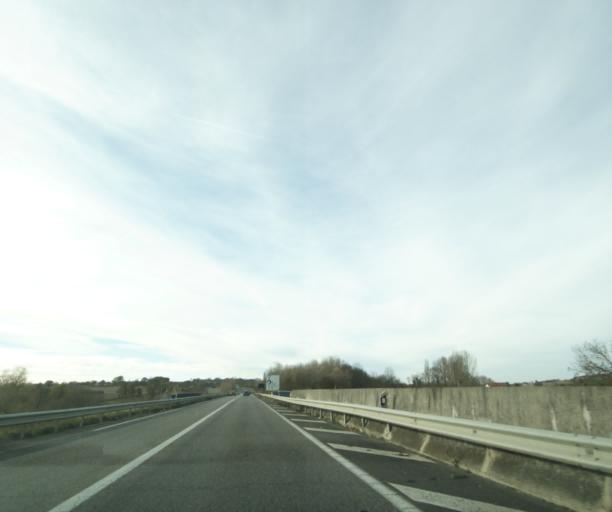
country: FR
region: Midi-Pyrenees
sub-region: Departement du Gers
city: Pujaudran
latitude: 43.6031
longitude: 1.0514
